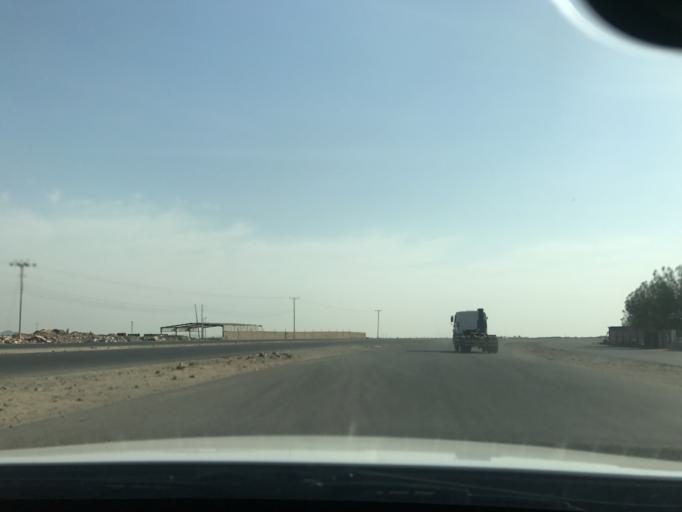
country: SA
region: Makkah
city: Al Jumum
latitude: 21.4429
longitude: 39.5167
